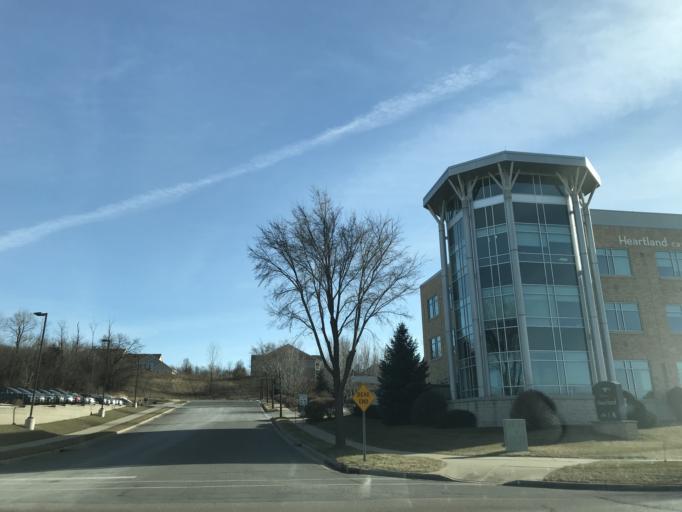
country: US
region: Wisconsin
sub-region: Dane County
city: Sun Prairie
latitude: 43.1406
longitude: -89.2871
